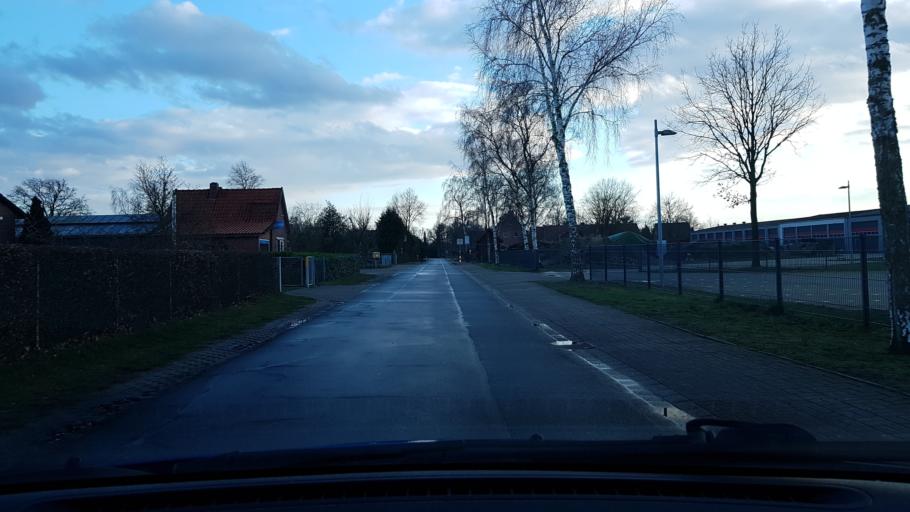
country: DE
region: Lower Saxony
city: Echem
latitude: 53.3385
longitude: 10.5432
